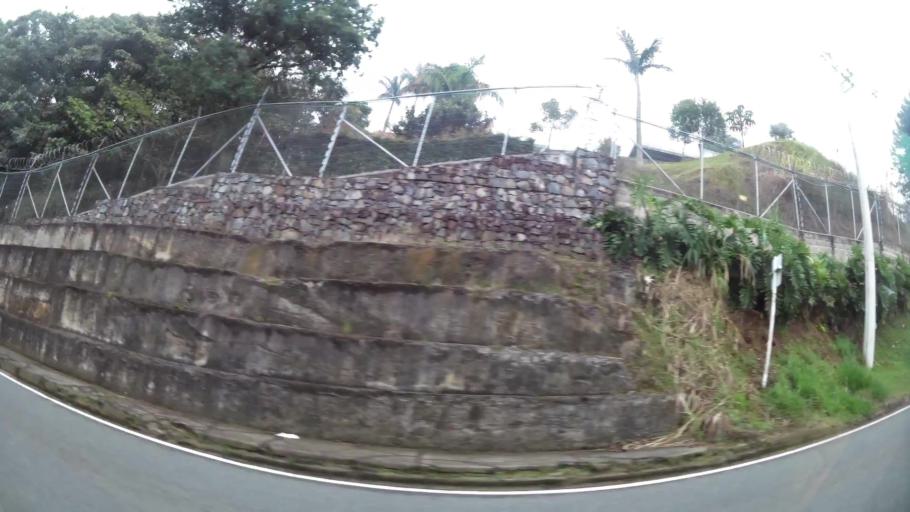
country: CO
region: Antioquia
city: Envigado
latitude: 6.1855
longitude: -75.5476
